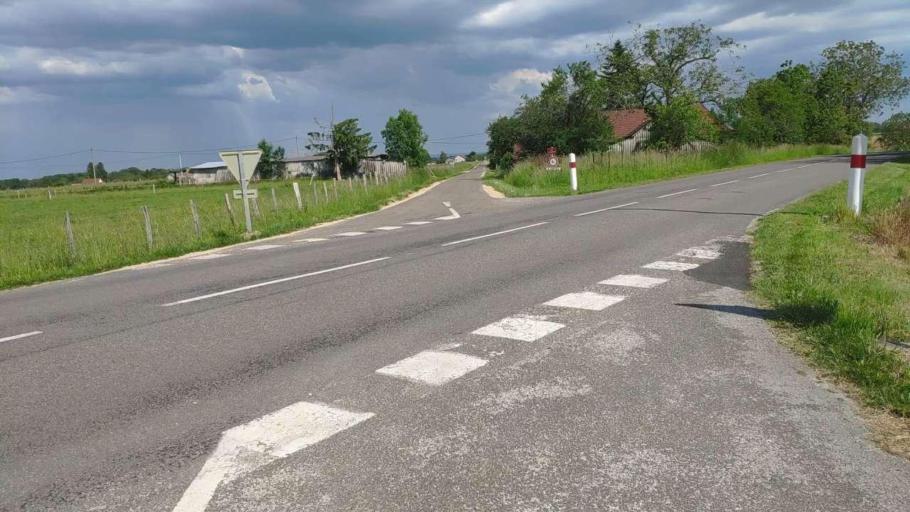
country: FR
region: Franche-Comte
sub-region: Departement du Jura
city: Bletterans
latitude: 46.8143
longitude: 5.3905
